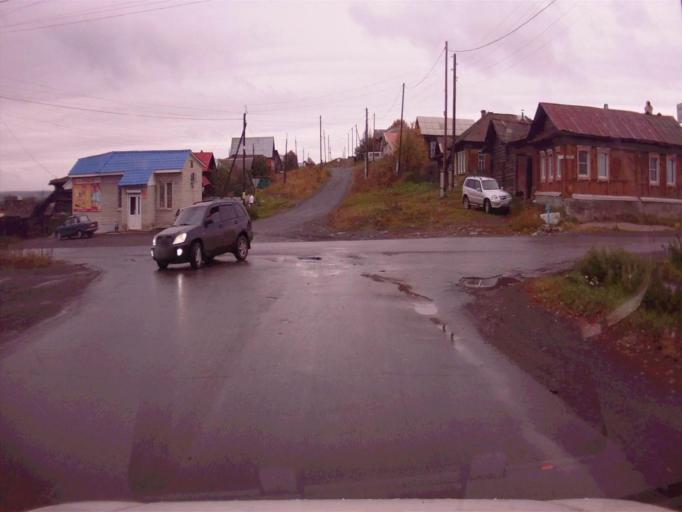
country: RU
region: Chelyabinsk
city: Verkhniy Ufaley
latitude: 56.0583
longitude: 60.2042
